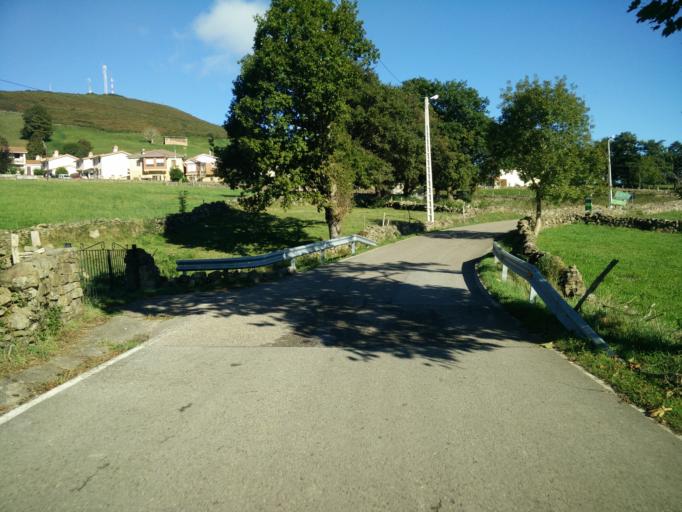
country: ES
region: Cantabria
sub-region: Provincia de Cantabria
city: San Pedro del Romeral
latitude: 43.1163
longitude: -3.8153
